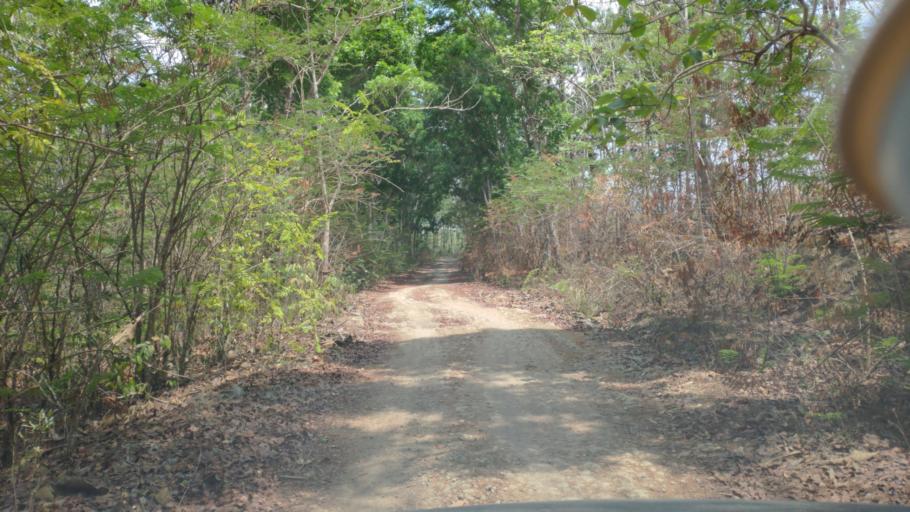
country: ID
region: Central Java
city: Singonegoro
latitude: -6.9902
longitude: 111.5402
